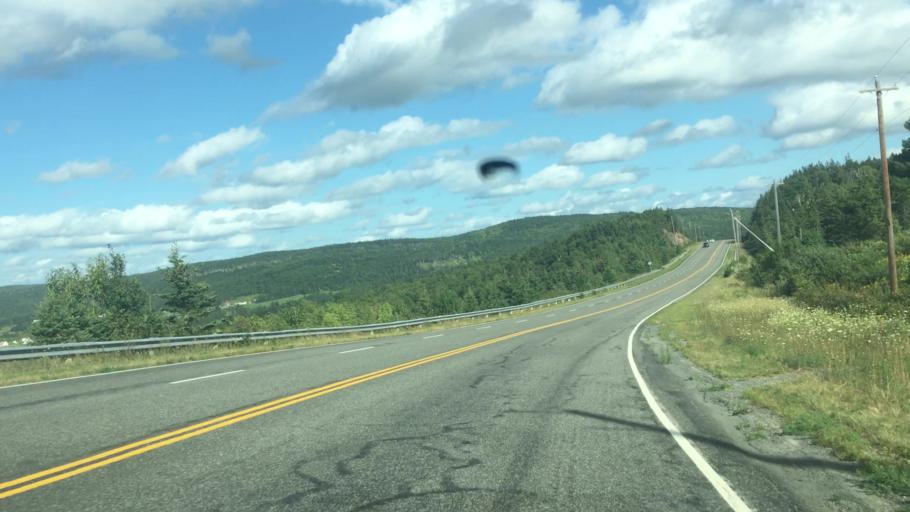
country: CA
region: Nova Scotia
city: Sydney
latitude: 45.8154
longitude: -60.6895
